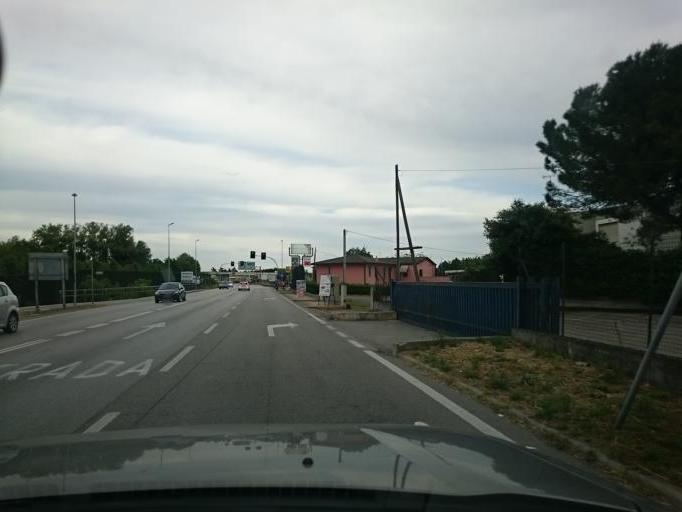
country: IT
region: Veneto
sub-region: Provincia di Padova
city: Monselice
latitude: 45.2333
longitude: 11.7576
